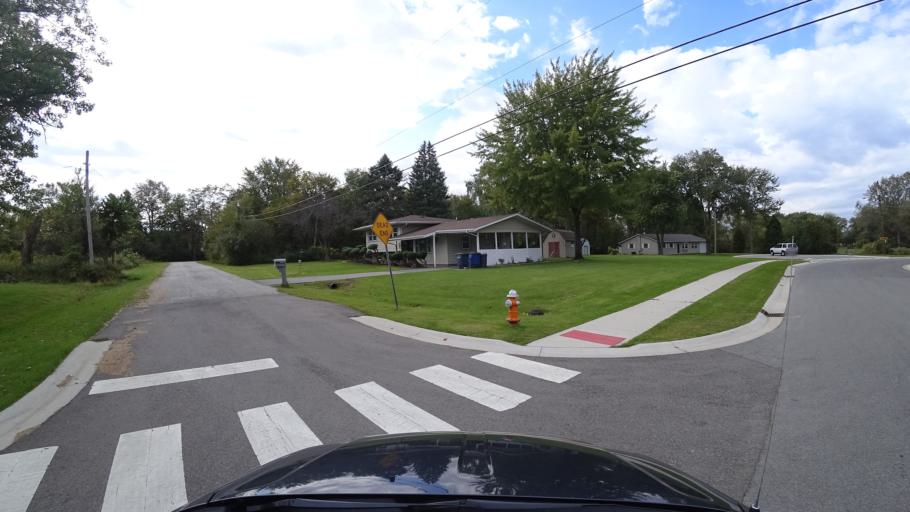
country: US
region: Indiana
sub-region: LaPorte County
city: Michigan City
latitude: 41.6716
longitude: -86.8966
